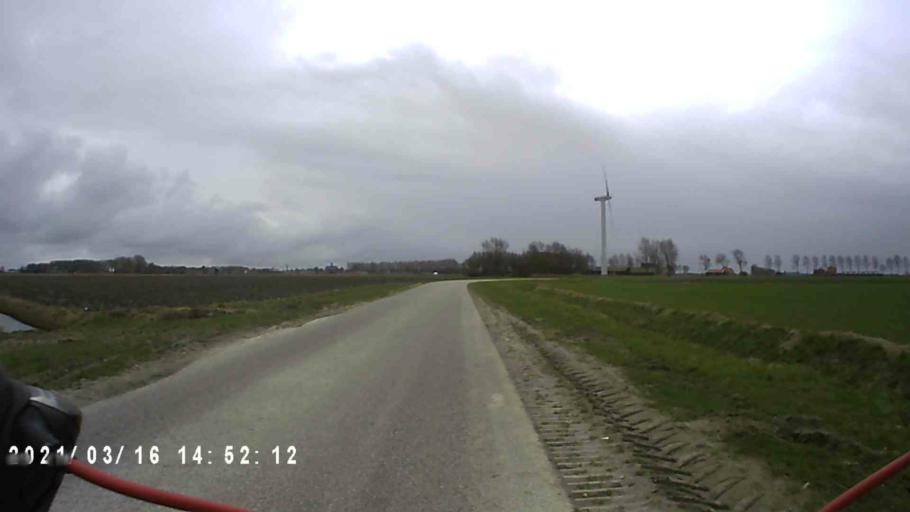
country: NL
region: Friesland
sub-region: Gemeente Harlingen
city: Harlingen
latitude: 53.1137
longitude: 5.4632
